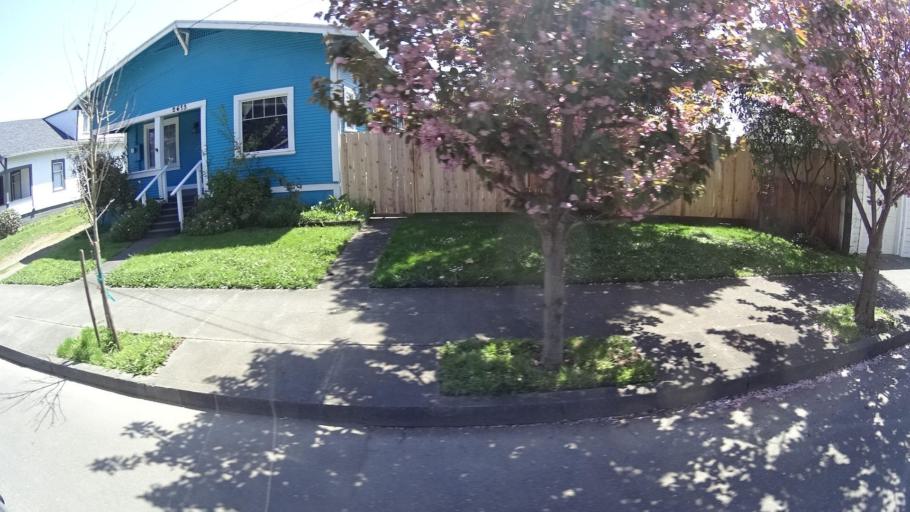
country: US
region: California
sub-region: Humboldt County
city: Bayview
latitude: 40.7843
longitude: -124.1809
